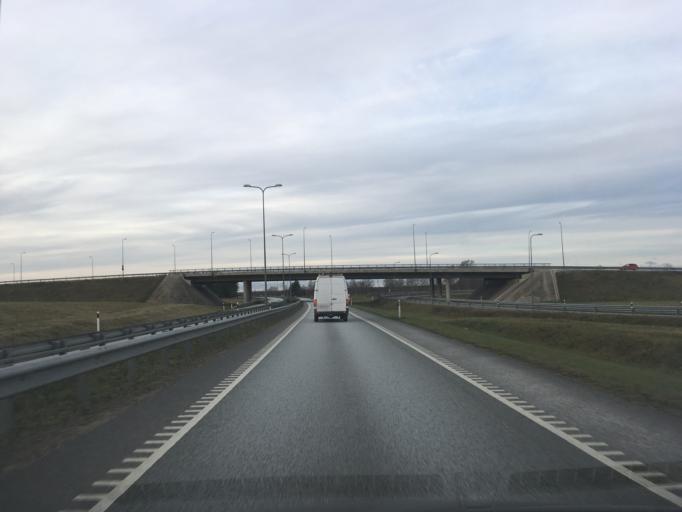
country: EE
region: Ida-Virumaa
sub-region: Kohtla-Jaerve linn
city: Kohtla-Jarve
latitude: 59.4025
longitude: 27.3284
